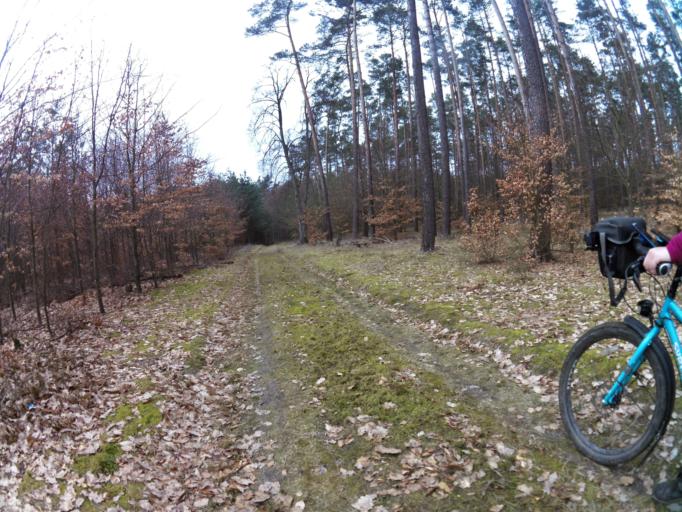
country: PL
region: Lubusz
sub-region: Powiat gorzowski
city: Witnica
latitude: 52.7680
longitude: 14.8295
